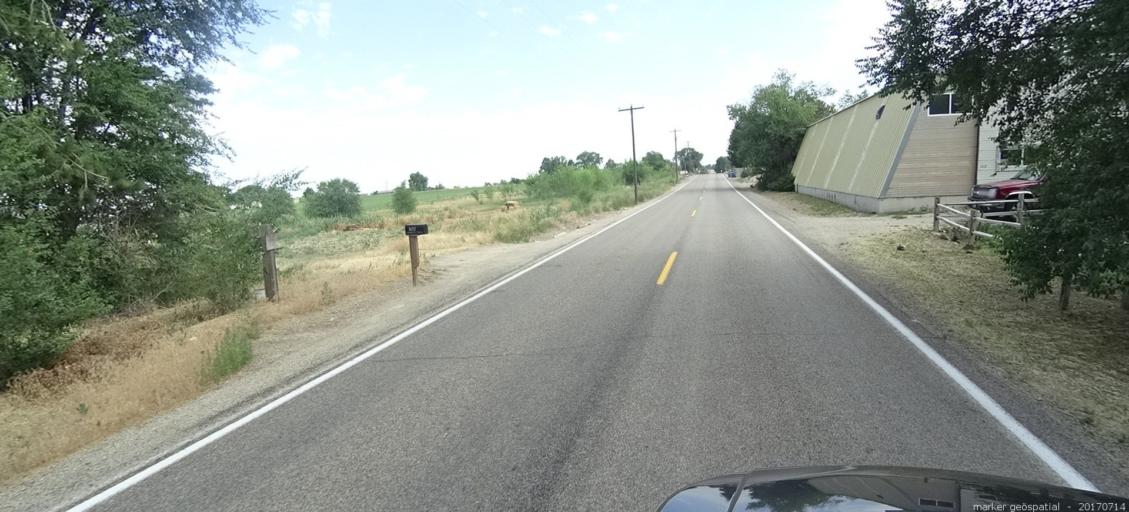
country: US
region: Idaho
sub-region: Ada County
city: Kuna
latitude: 43.4710
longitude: -116.3545
